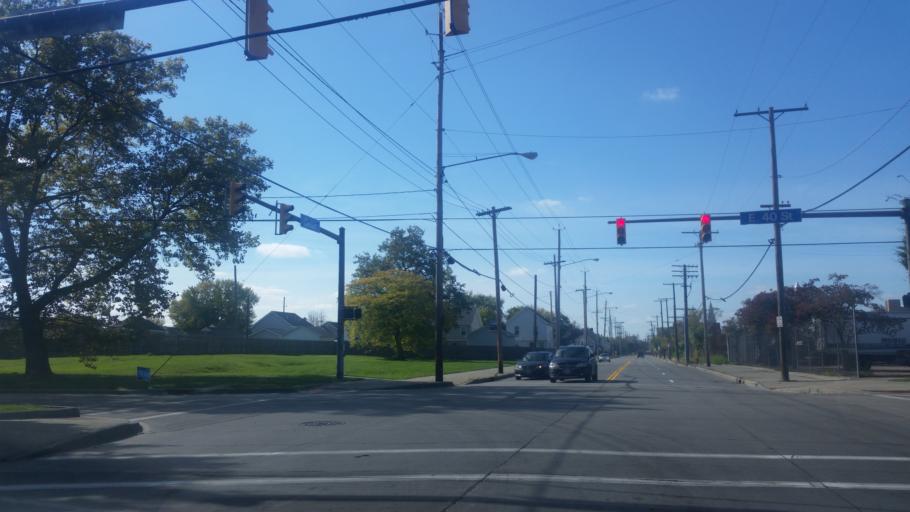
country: US
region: Ohio
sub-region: Cuyahoga County
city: Cleveland
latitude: 41.5000
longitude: -81.6569
